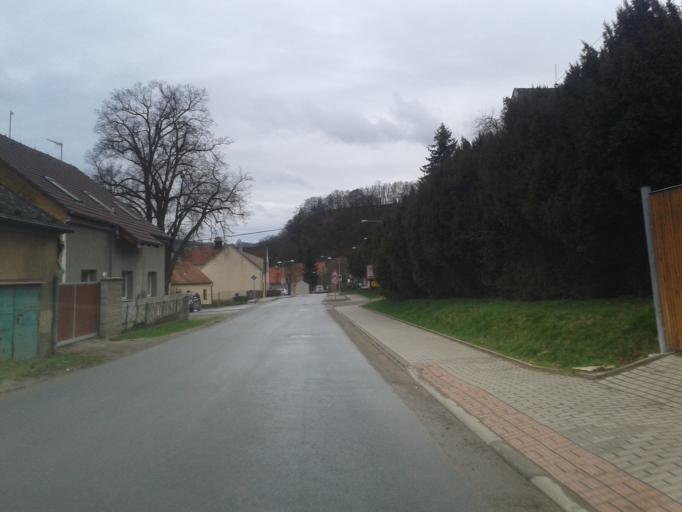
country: CZ
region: Central Bohemia
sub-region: Okres Beroun
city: Lodenice
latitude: 50.0053
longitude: 14.1524
